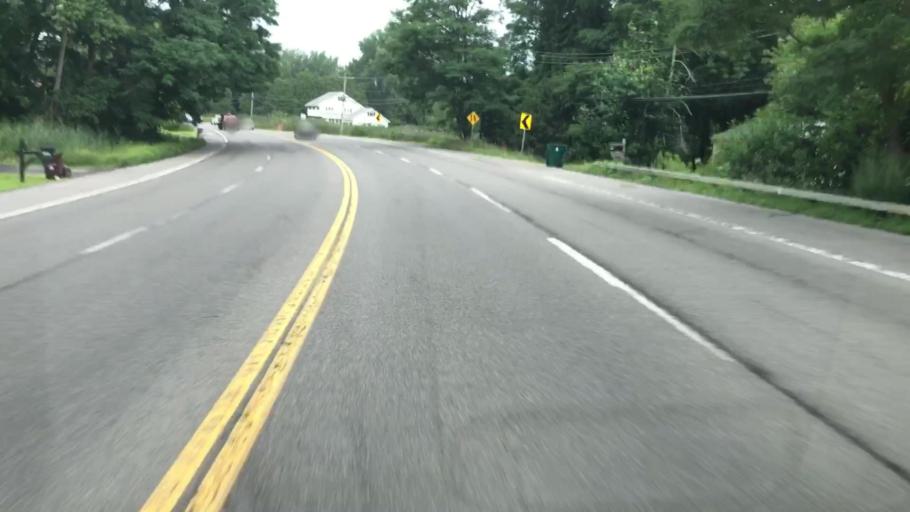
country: US
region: New York
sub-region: Onondaga County
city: Liverpool
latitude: 43.1749
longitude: -76.2096
